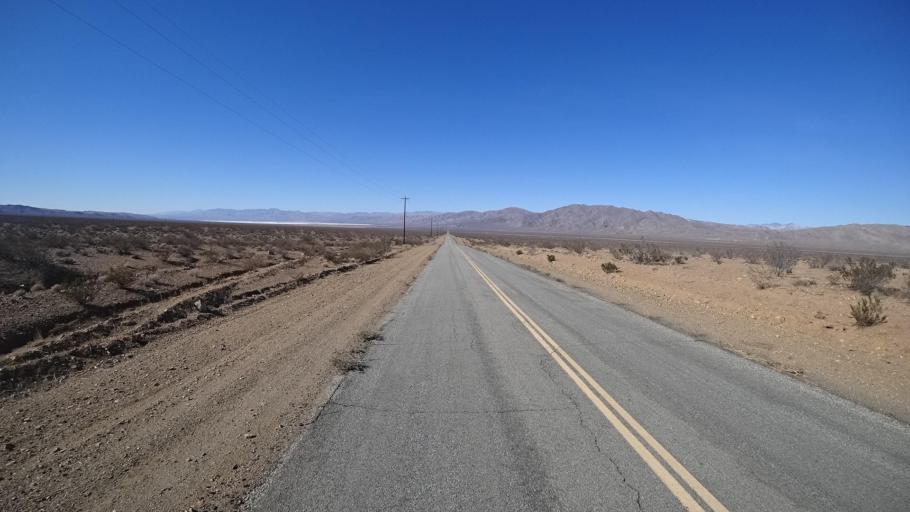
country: US
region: California
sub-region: Kern County
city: Ridgecrest
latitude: 35.3831
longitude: -117.7045
